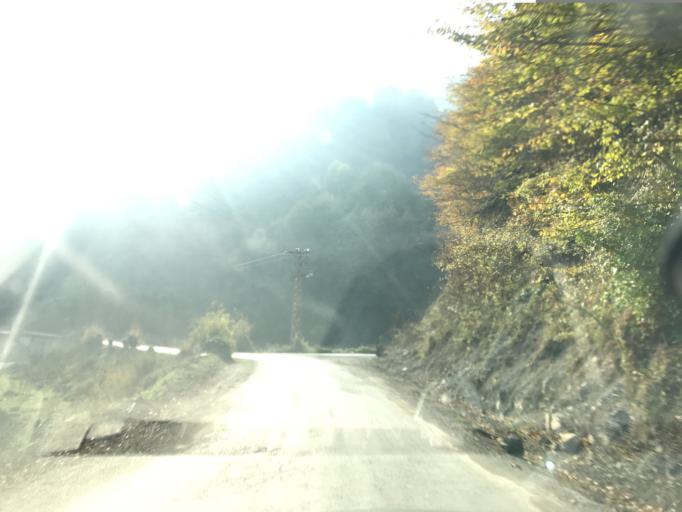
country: TR
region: Duzce
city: Cumayeri
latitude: 40.9299
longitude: 30.9256
